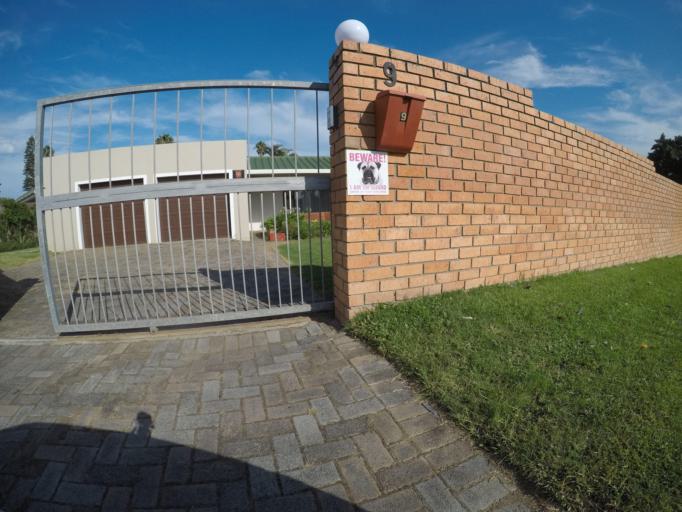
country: ZA
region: Eastern Cape
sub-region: Buffalo City Metropolitan Municipality
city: East London
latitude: -32.9454
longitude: 28.0039
